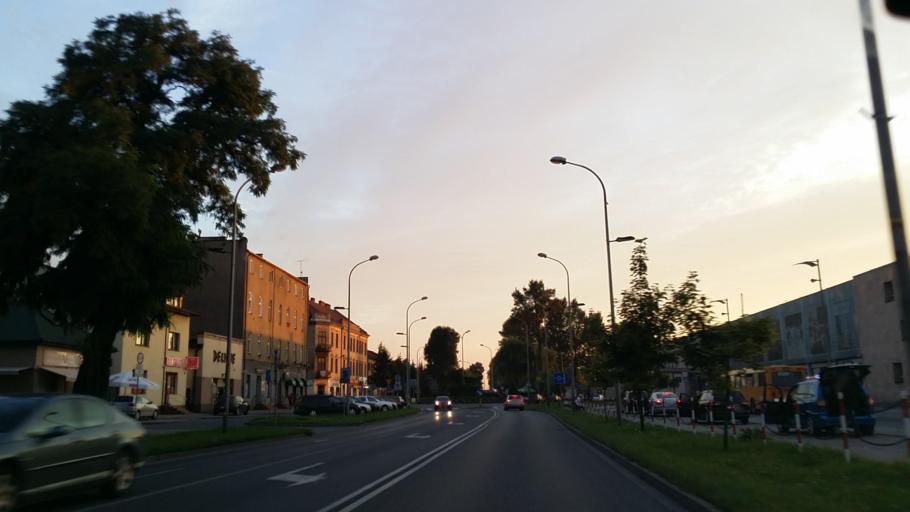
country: PL
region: Lesser Poland Voivodeship
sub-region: Powiat oswiecimski
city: Brzezinka
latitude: 50.0417
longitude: 19.2014
